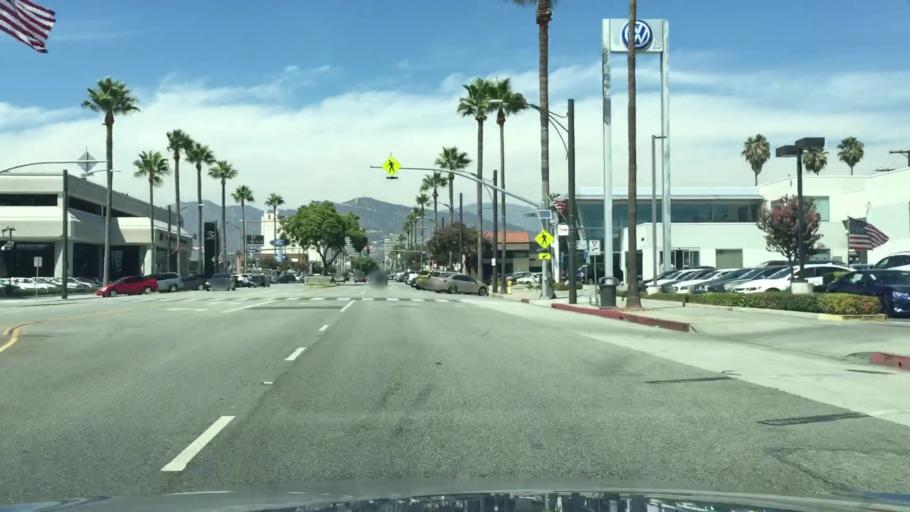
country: US
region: California
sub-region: Los Angeles County
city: Glendale
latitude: 34.1308
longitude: -118.2548
